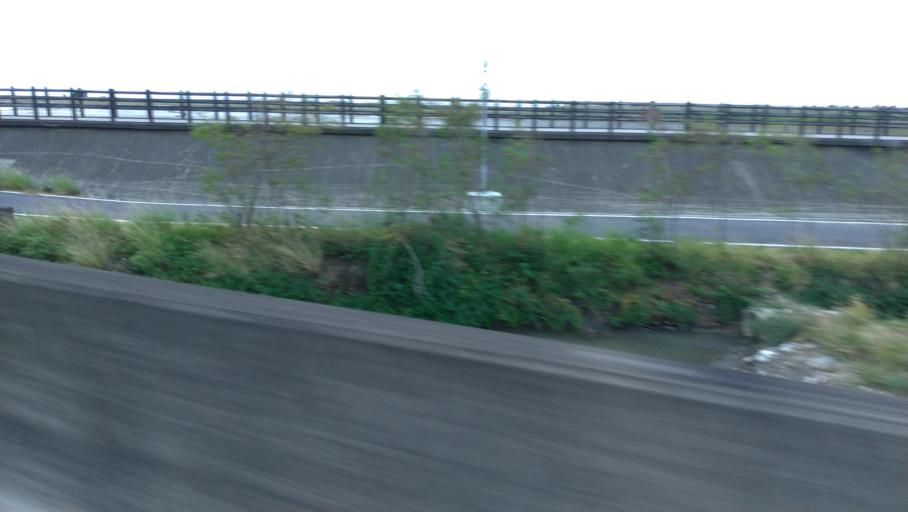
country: TW
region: Taiwan
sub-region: Hsinchu
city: Hsinchu
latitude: 24.7590
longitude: 120.9065
